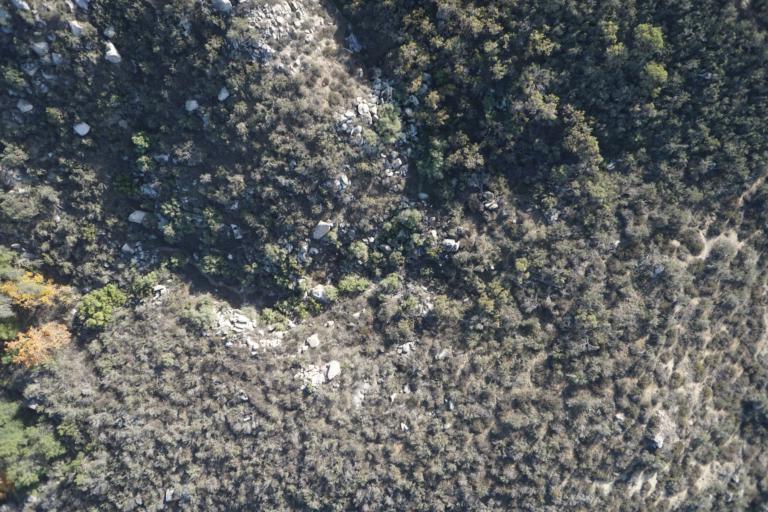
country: US
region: California
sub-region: Riverside County
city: East Hemet
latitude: 33.6412
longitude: -116.9253
